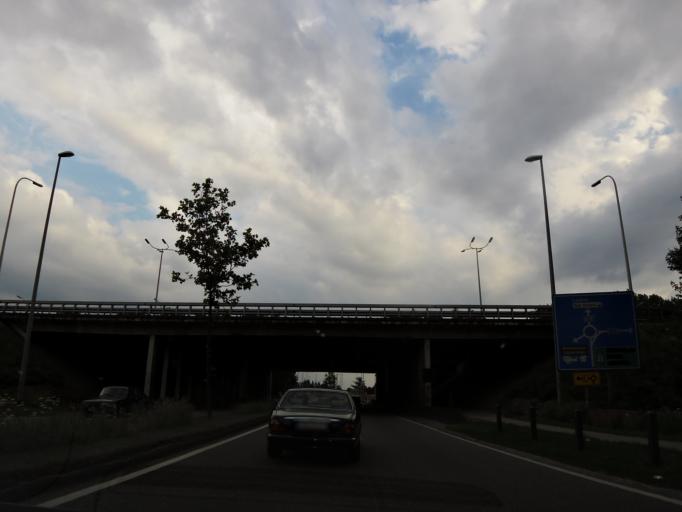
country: BE
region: Flanders
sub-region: Provincie Limburg
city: Maasmechelen
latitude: 50.9540
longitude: 5.6940
